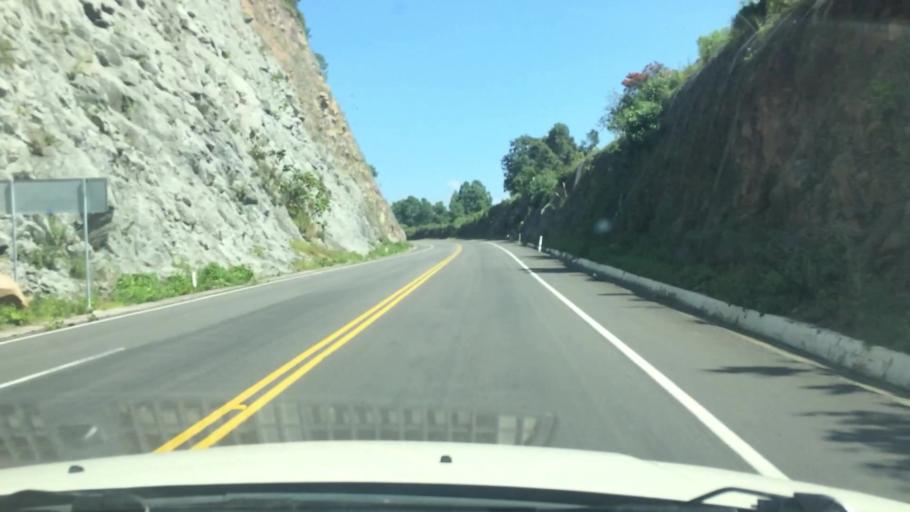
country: MX
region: Mexico
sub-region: Amanalco
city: San Bartolo
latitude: 19.2432
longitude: -100.0662
